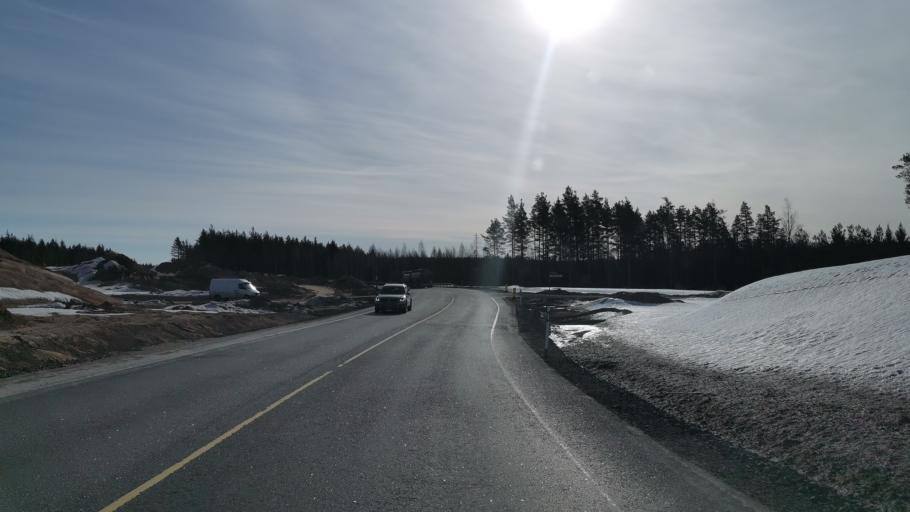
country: FI
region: Kymenlaakso
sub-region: Kouvola
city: Elimaeki
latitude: 60.8732
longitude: 26.4977
